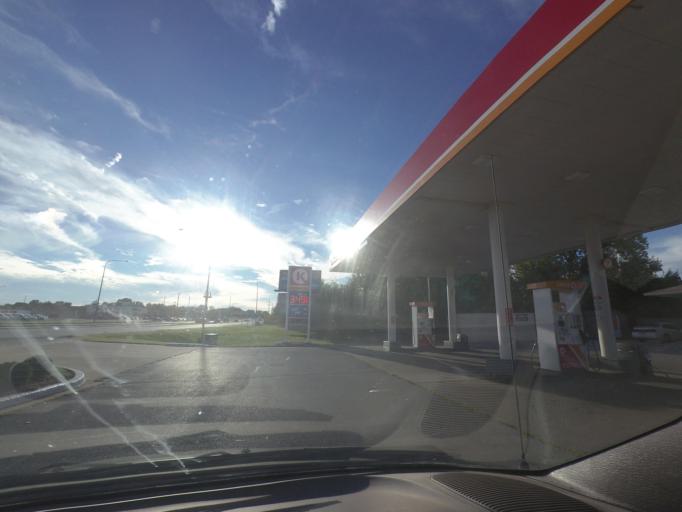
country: US
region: Illinois
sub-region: Sangamon County
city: Grandview
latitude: 39.8021
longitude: -89.6017
